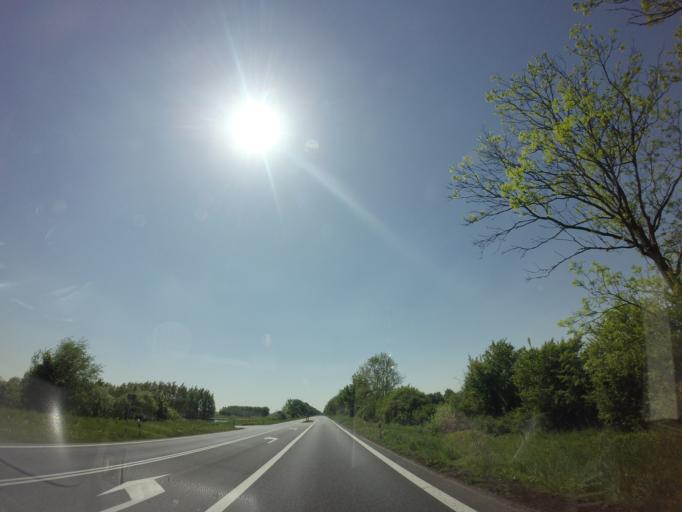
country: PL
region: West Pomeranian Voivodeship
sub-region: Powiat pyrzycki
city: Lipiany
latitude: 52.9732
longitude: 14.9732
